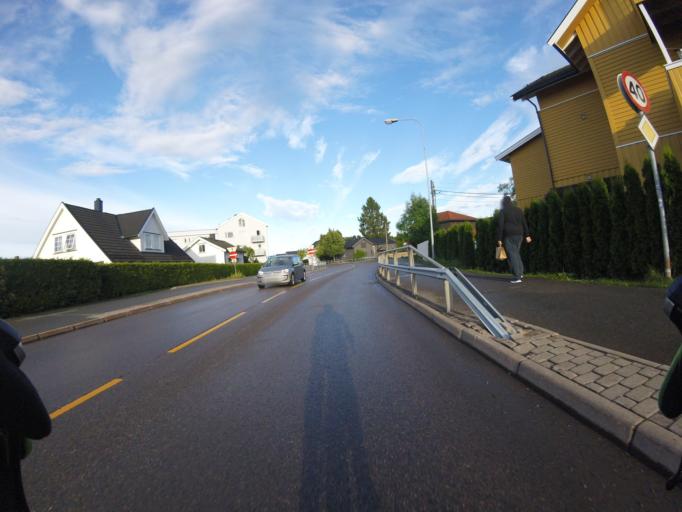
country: NO
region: Akershus
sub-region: Skedsmo
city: Lillestrom
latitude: 59.9548
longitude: 11.0582
